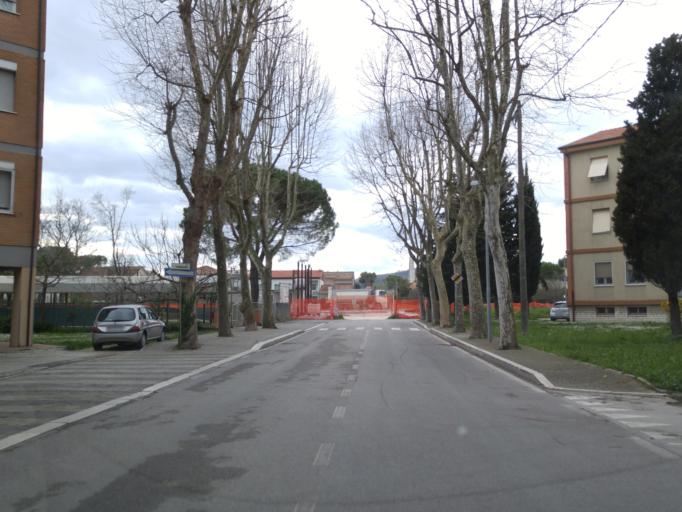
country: IT
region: The Marches
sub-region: Provincia di Pesaro e Urbino
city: Fano
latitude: 43.8391
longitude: 13.0038
